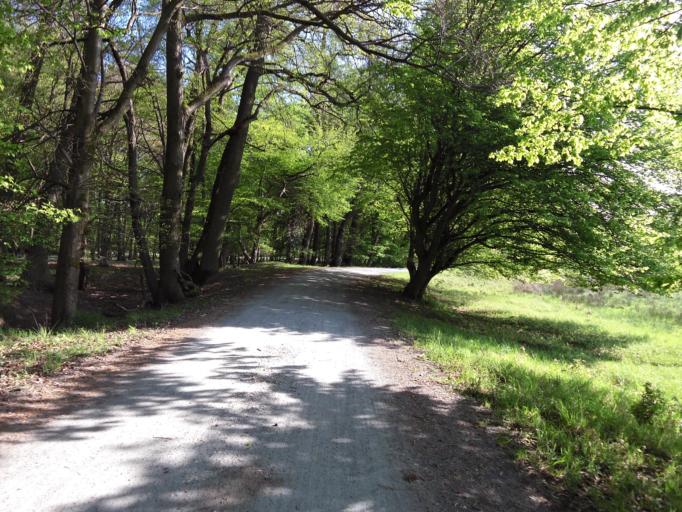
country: DE
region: Hesse
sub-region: Regierungsbezirk Darmstadt
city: Nauheim
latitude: 49.9772
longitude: 8.5194
